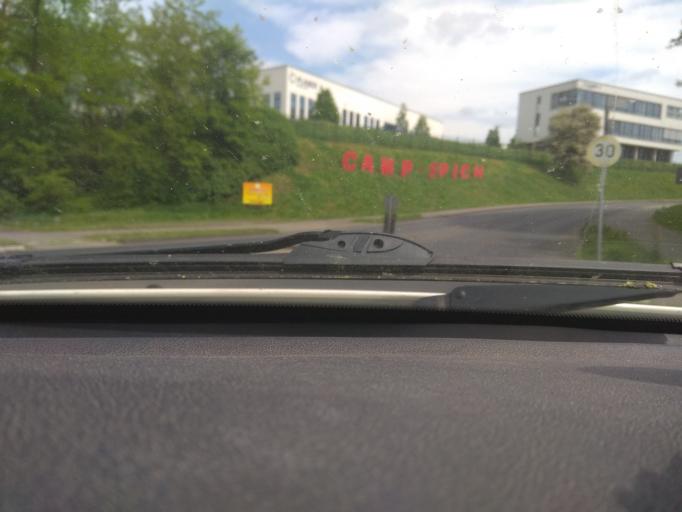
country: DE
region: North Rhine-Westphalia
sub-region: Regierungsbezirk Koln
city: Wahn-Heide
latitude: 50.8392
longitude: 7.1169
